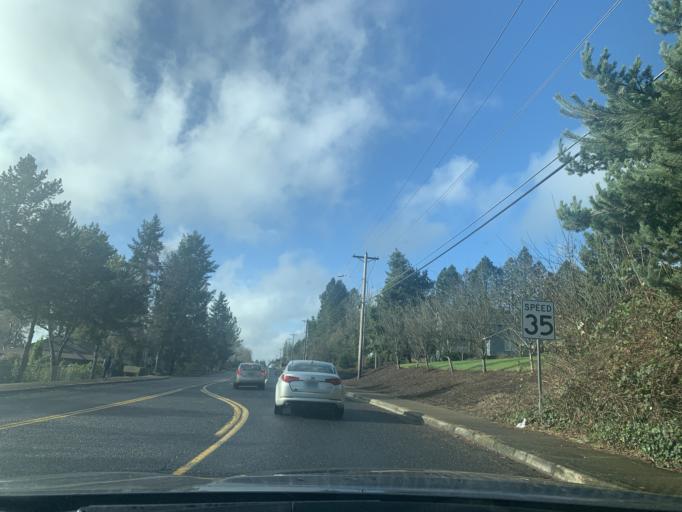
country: US
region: Oregon
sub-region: Washington County
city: King City
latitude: 45.4114
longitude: -122.7961
